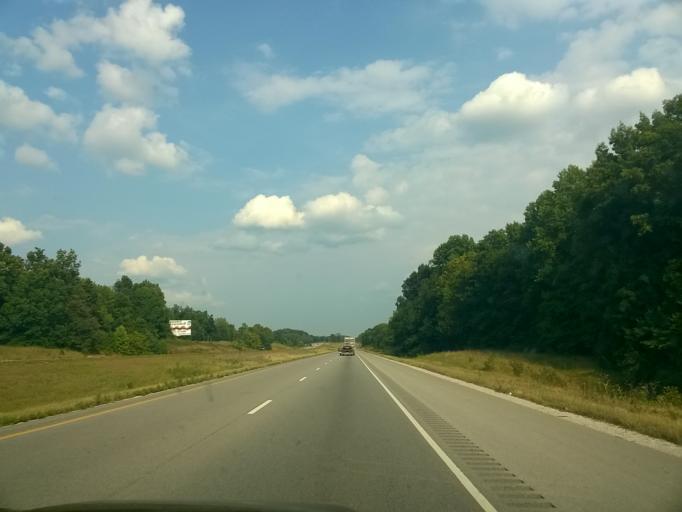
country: US
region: Indiana
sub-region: Vigo County
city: Seelyville
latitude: 39.4457
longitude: -87.2232
